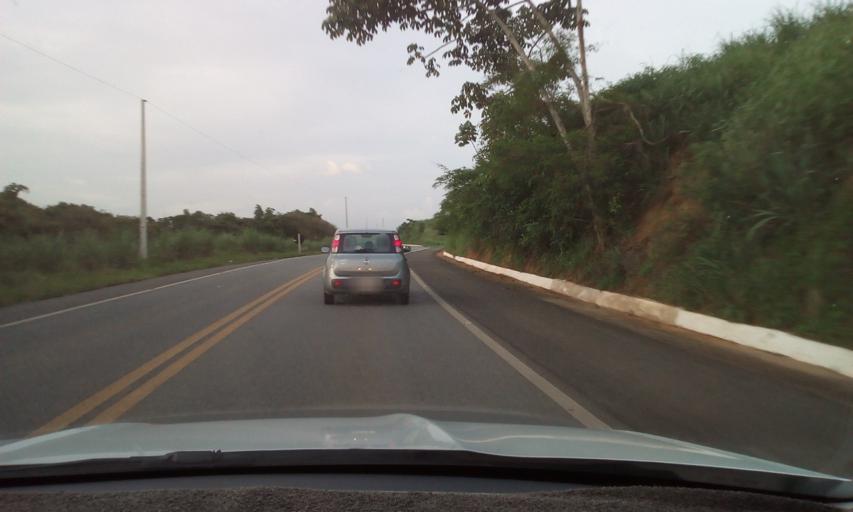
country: BR
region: Pernambuco
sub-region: Vicencia
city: Vicencia
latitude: -7.6398
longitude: -35.2543
